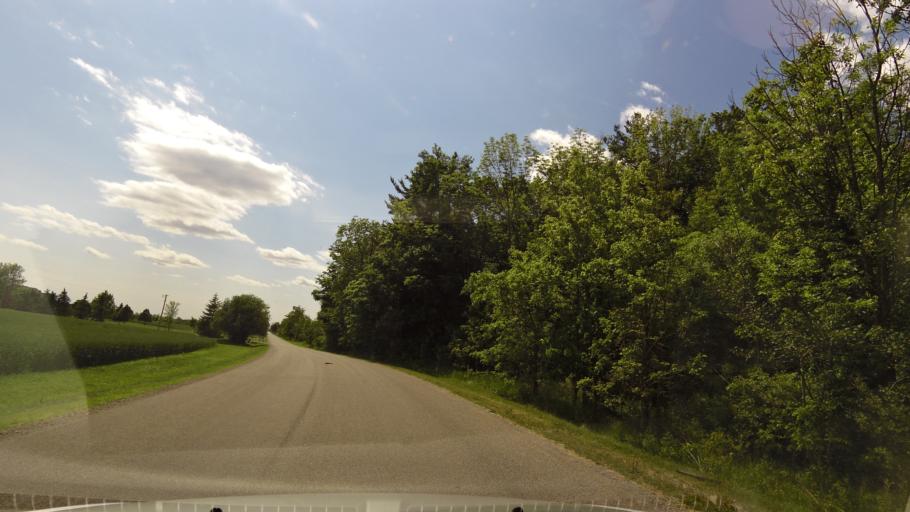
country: CA
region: Ontario
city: Ancaster
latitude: 43.1579
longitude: -80.0563
